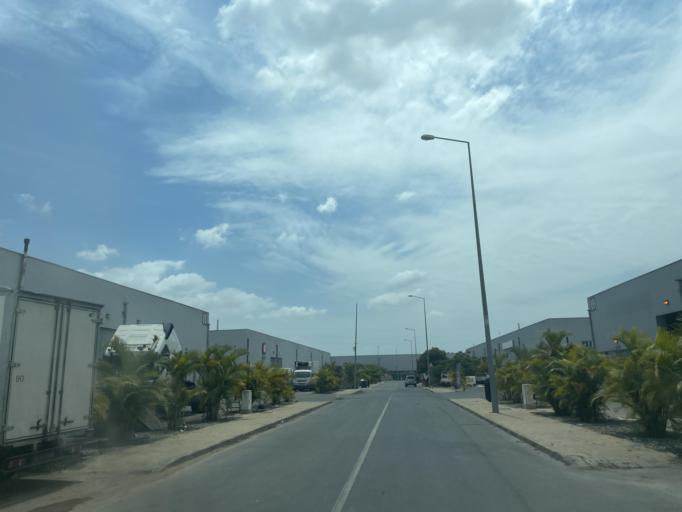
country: AO
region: Luanda
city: Luanda
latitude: -8.9592
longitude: 13.3911
